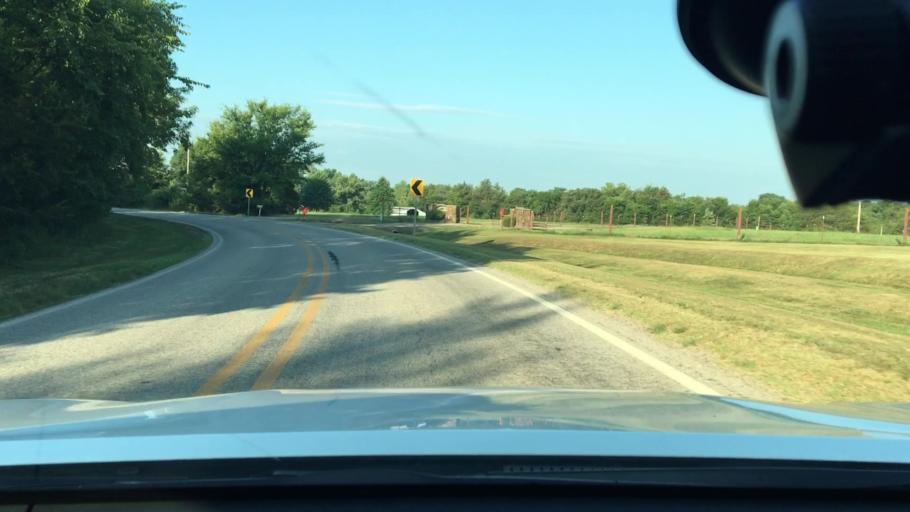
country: US
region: Arkansas
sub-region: Johnson County
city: Coal Hill
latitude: 35.3461
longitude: -93.5948
